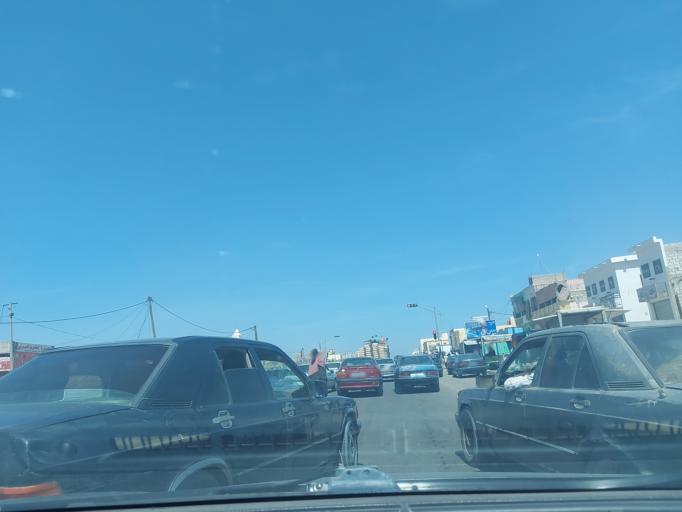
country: MR
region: Nouakchott
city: Nouakchott
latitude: 18.0736
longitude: -15.9450
